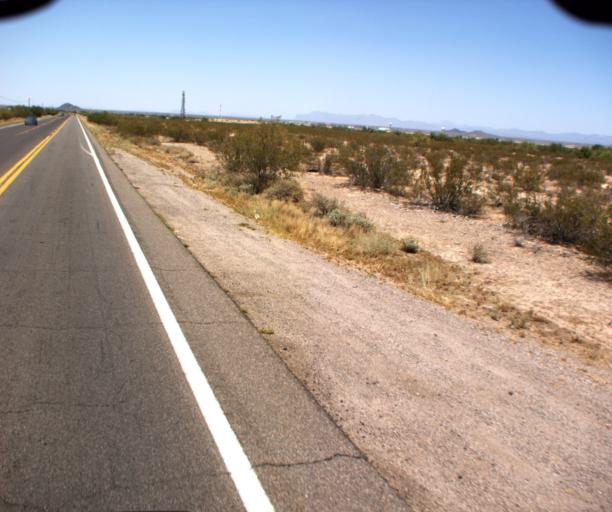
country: US
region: Arizona
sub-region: Pinal County
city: Florence
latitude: 33.0023
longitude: -111.3715
